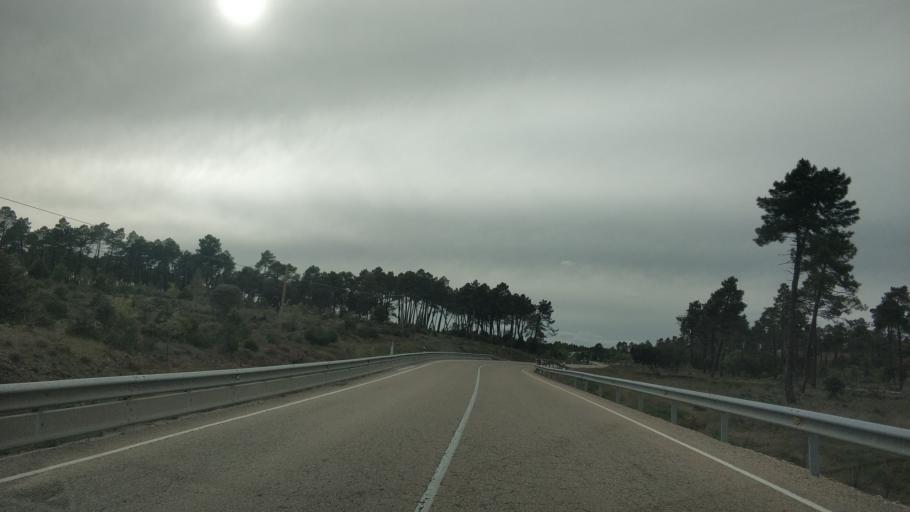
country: ES
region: Castille and Leon
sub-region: Provincia de Soria
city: Bayubas de Abajo
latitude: 41.5206
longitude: -2.9332
